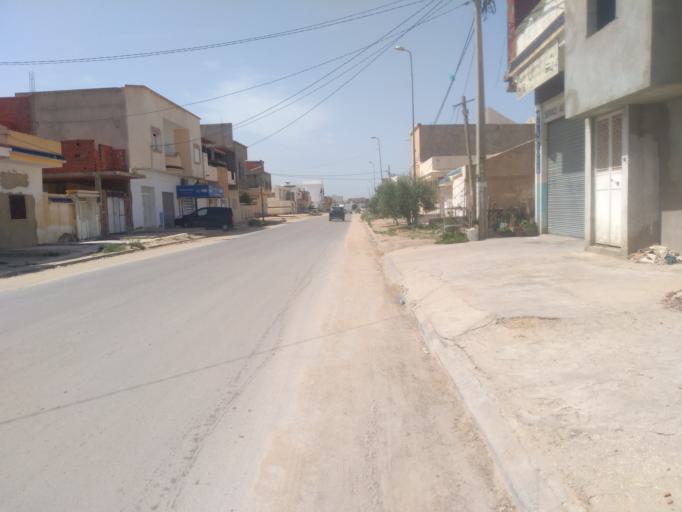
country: TN
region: Al Qayrawan
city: Kairouan
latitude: 35.6649
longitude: 10.0788
